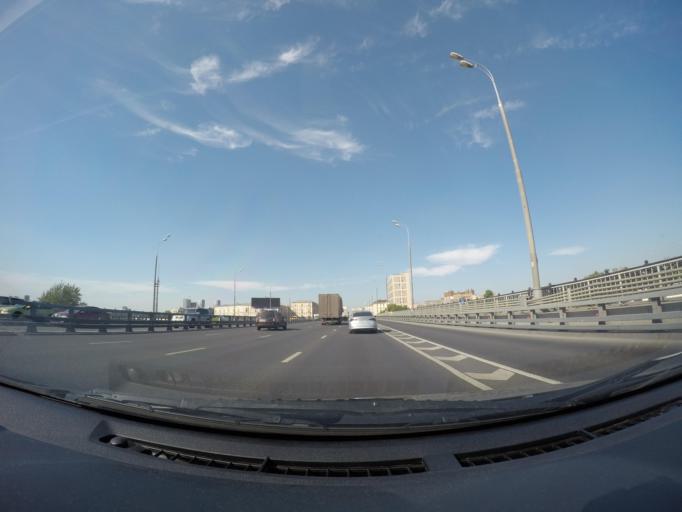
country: RU
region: Moscow
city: Mar'ina Roshcha
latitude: 55.7972
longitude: 37.6350
